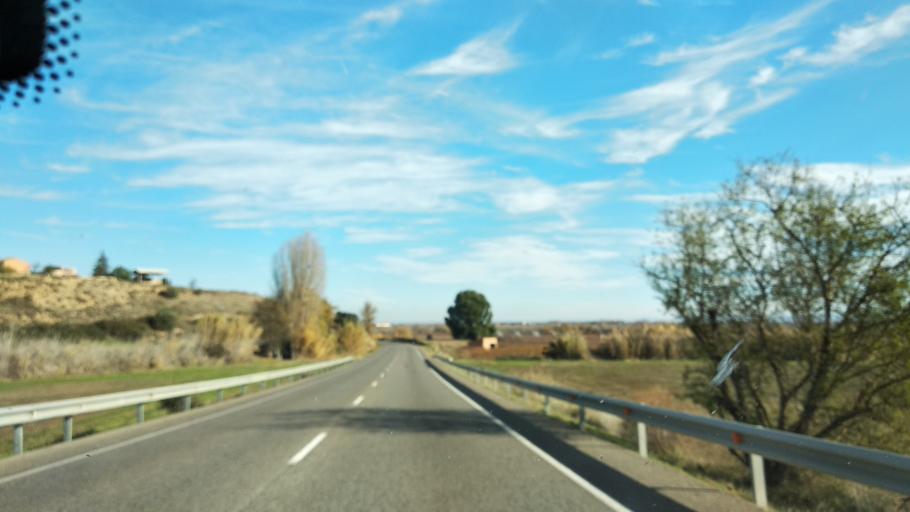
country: ES
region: Catalonia
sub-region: Provincia de Lleida
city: Corbins
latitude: 41.6821
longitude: 0.6873
